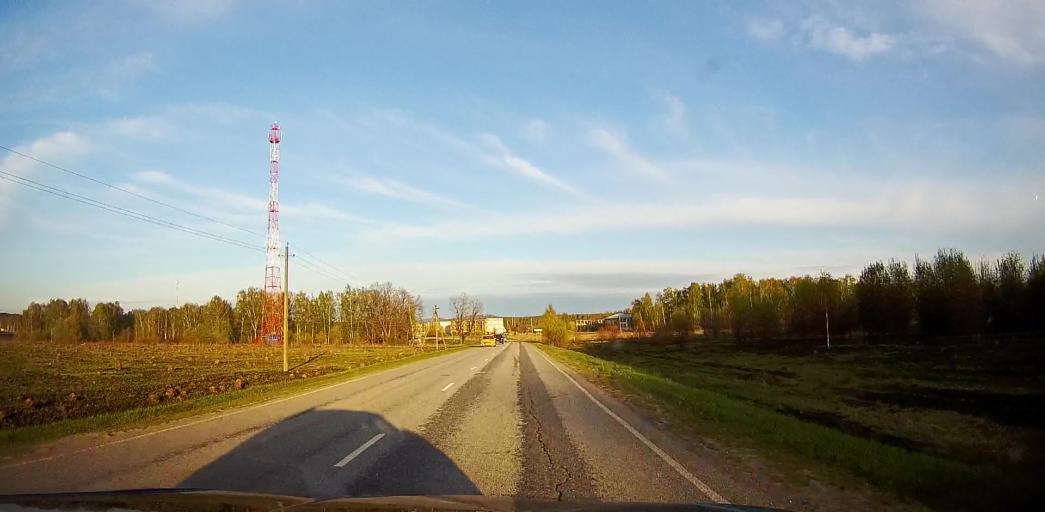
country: RU
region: Moskovskaya
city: Meshcherino
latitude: 55.2348
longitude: 38.3557
